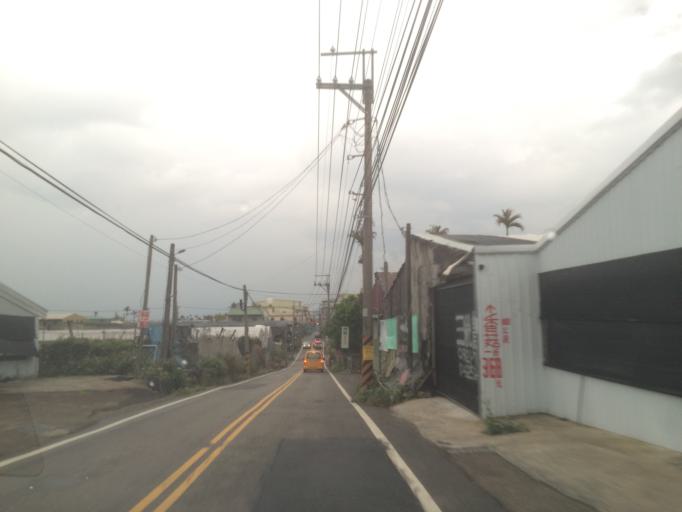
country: TW
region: Taiwan
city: Fengyuan
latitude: 24.1795
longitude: 120.8210
